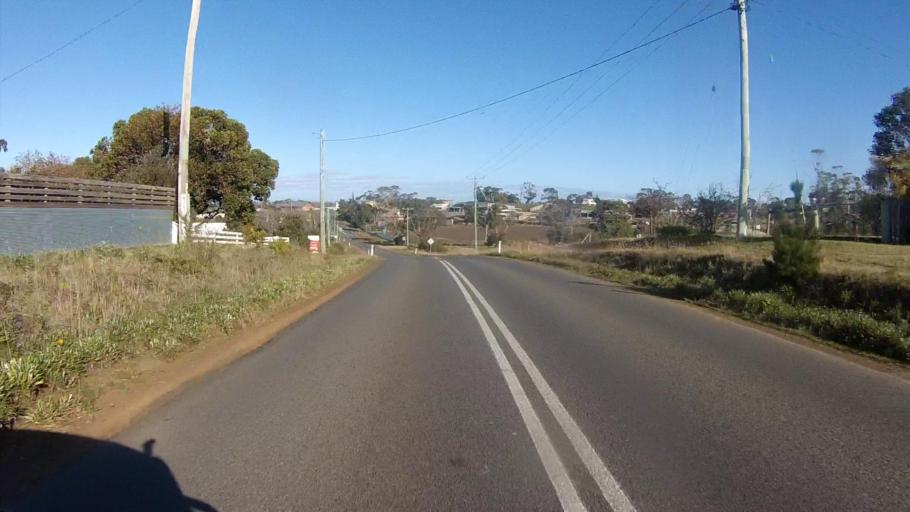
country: AU
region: Tasmania
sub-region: Sorell
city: Sorell
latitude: -42.8819
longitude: 147.8173
